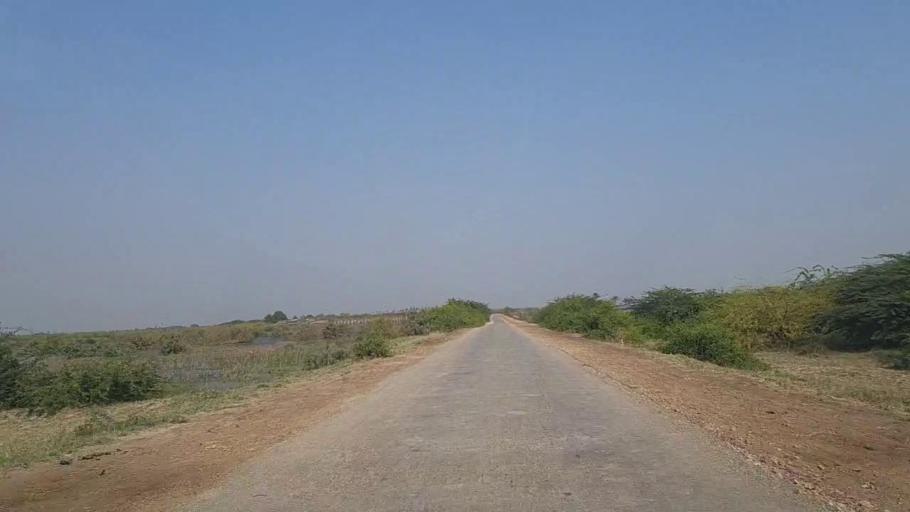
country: PK
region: Sindh
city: Keti Bandar
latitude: 24.2460
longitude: 67.7100
